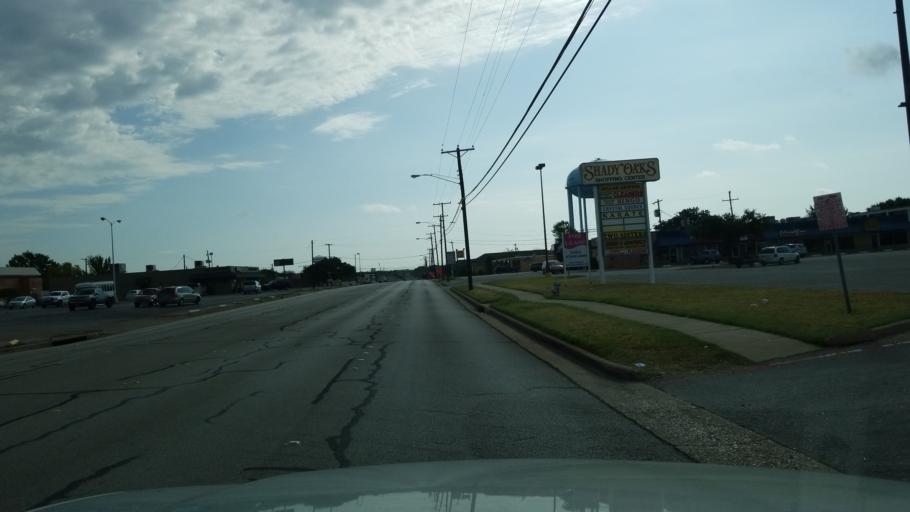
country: US
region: Texas
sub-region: Tarrant County
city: Hurst
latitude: 32.8339
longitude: -97.1757
